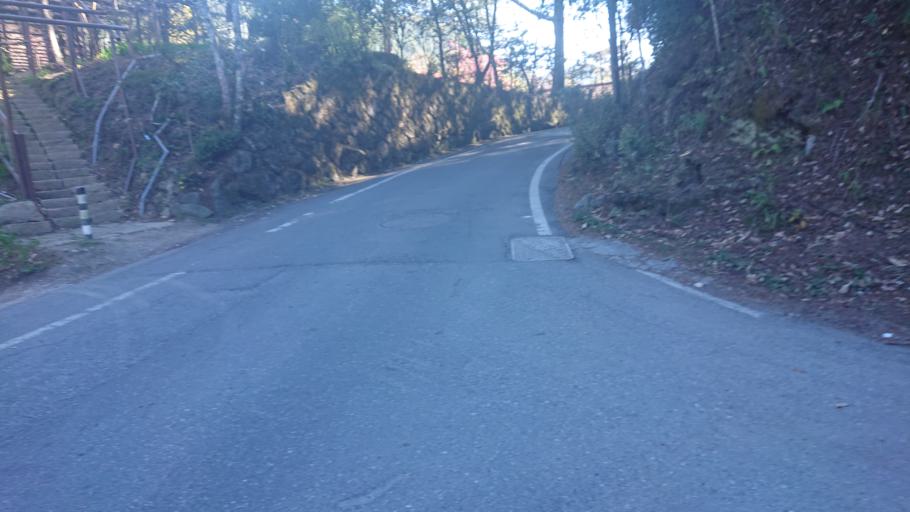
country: TW
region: Taiwan
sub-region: Hualien
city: Hualian
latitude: 24.3561
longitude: 121.3123
